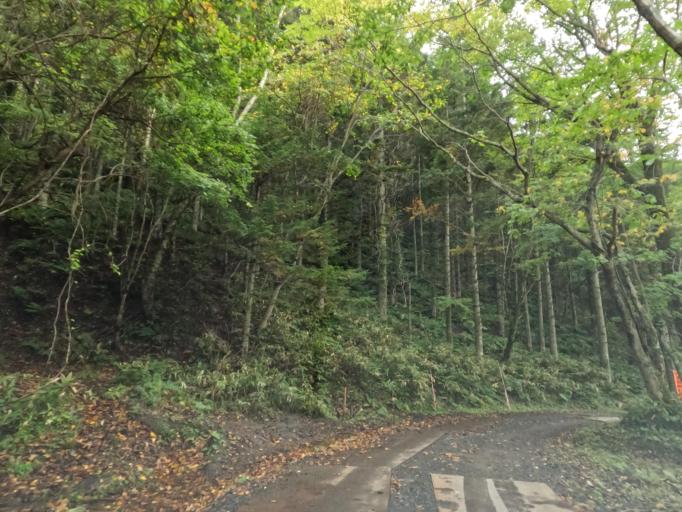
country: JP
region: Hokkaido
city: Date
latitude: 42.4971
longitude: 140.9304
